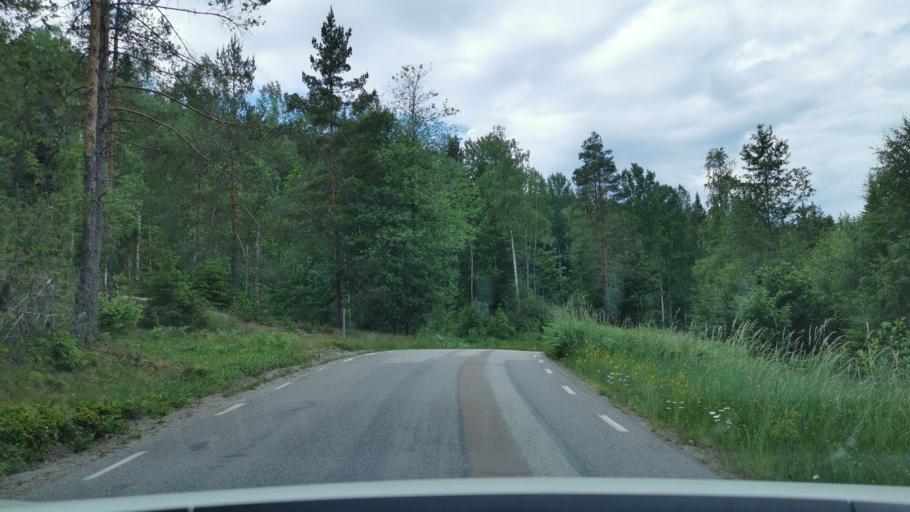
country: SE
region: Vaestra Goetaland
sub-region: Bengtsfors Kommun
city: Dals Langed
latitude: 58.8596
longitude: 12.4028
